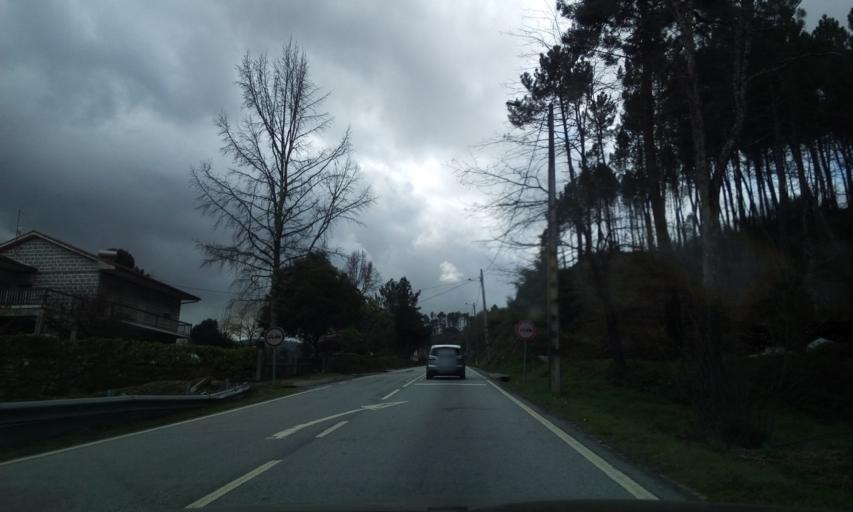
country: PT
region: Viseu
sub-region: Mangualde
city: Mangualde
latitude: 40.6403
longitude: -7.7393
